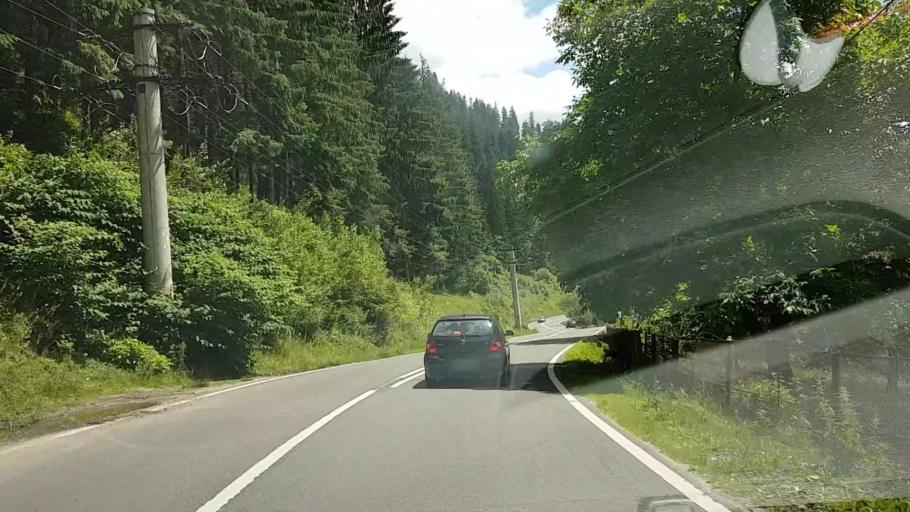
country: RO
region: Suceava
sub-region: Comuna Brosteni
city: Brosteni
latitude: 47.2702
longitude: 25.6523
